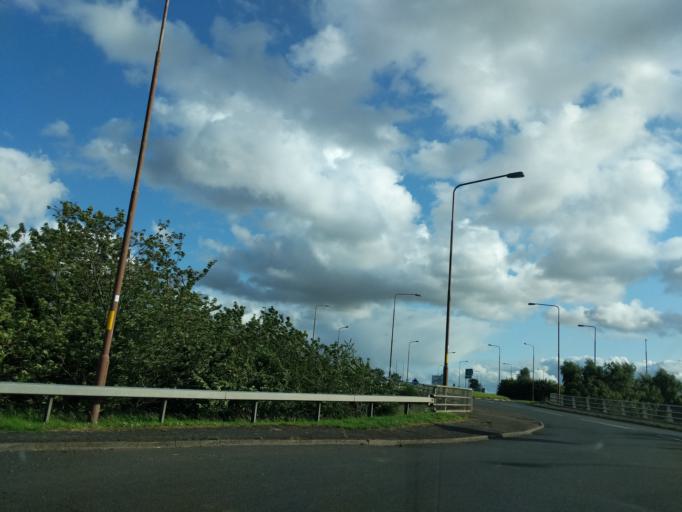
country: GB
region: Scotland
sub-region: East Lothian
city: Macmerry
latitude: 55.9508
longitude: -2.8801
